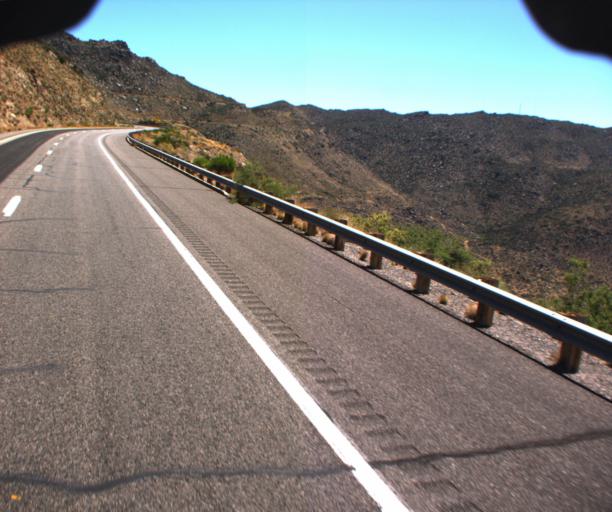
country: US
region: Arizona
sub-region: Yavapai County
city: Congress
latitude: 34.2008
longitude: -112.7798
